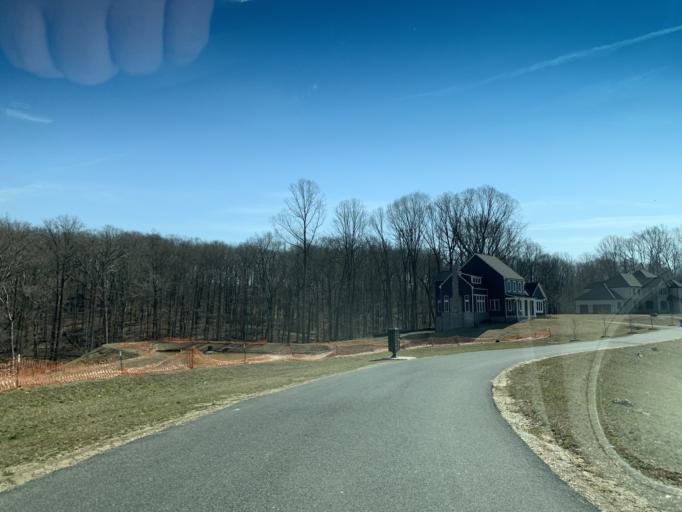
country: US
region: Maryland
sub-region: Harford County
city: Fallston
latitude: 39.5176
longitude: -76.4392
